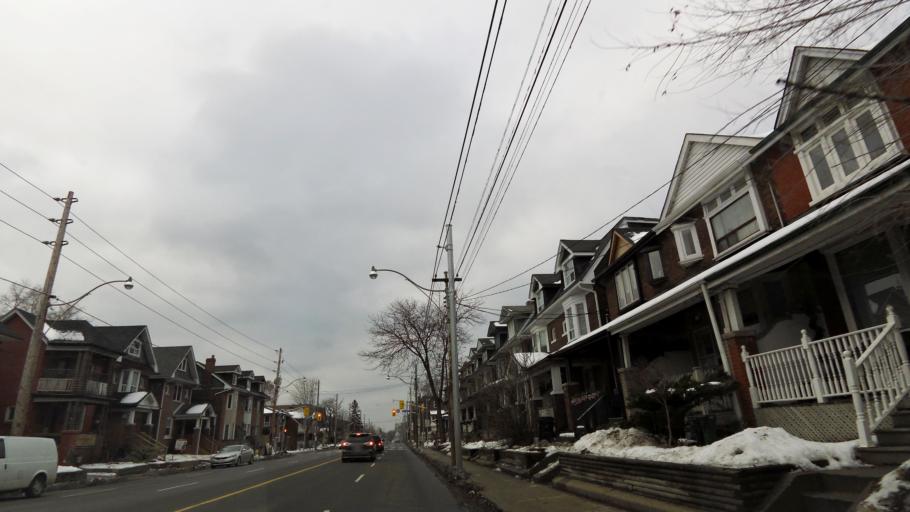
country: CA
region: Ontario
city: Scarborough
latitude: 43.6729
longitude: -79.3075
